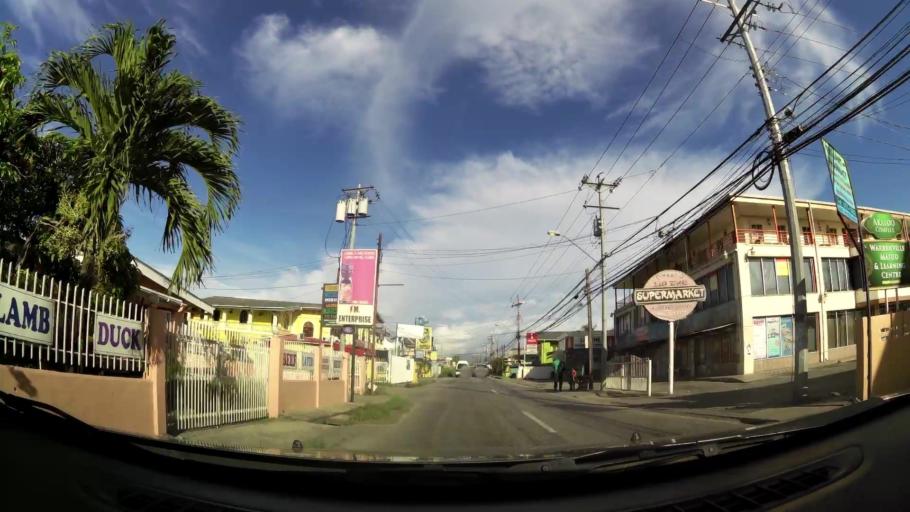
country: TT
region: Tunapuna/Piarco
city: Tunapuna
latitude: 10.5725
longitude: -61.3750
